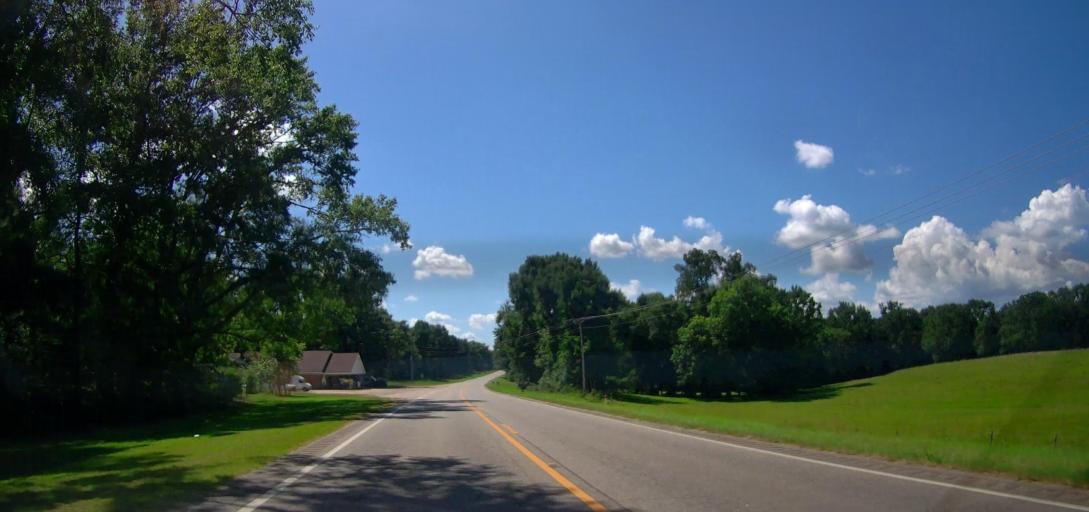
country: US
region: Alabama
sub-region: Elmore County
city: Tallassee
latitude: 32.3805
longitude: -85.8725
